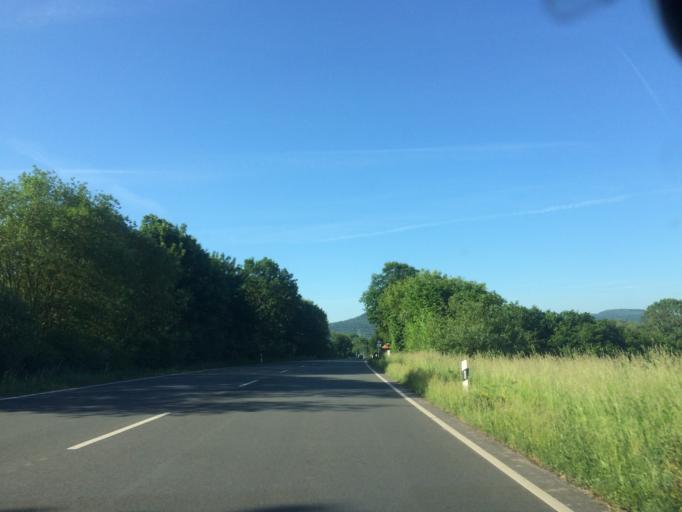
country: DE
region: Hesse
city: Trendelburg
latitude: 51.5515
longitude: 9.4162
